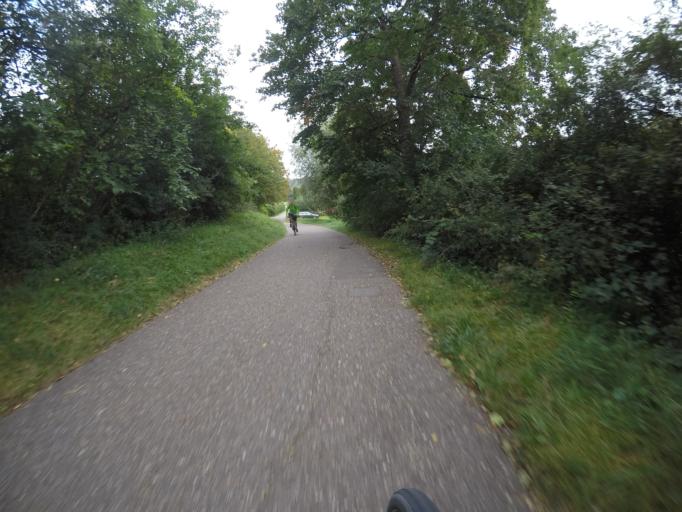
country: DE
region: Baden-Wuerttemberg
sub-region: Regierungsbezirk Stuttgart
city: Erdmannhausen
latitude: 48.8796
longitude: 9.2767
